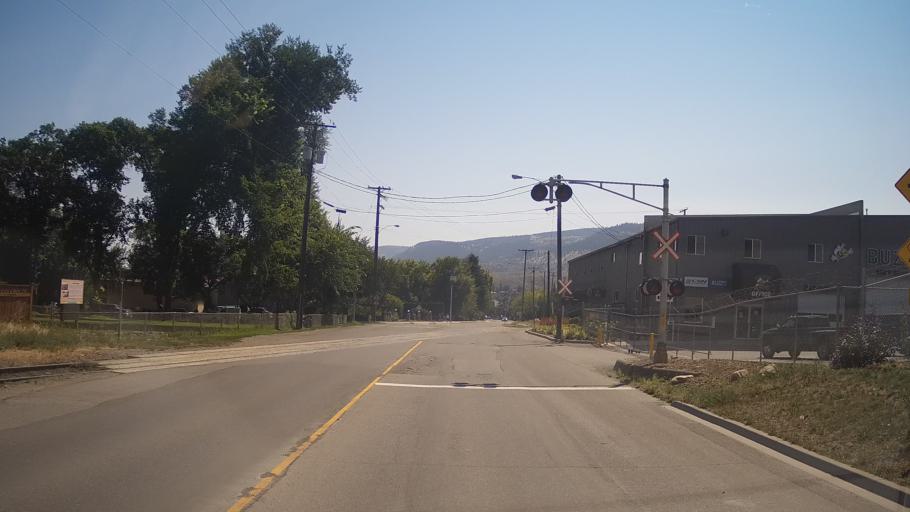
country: CA
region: British Columbia
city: Kamloops
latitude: 50.6774
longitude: -120.3215
